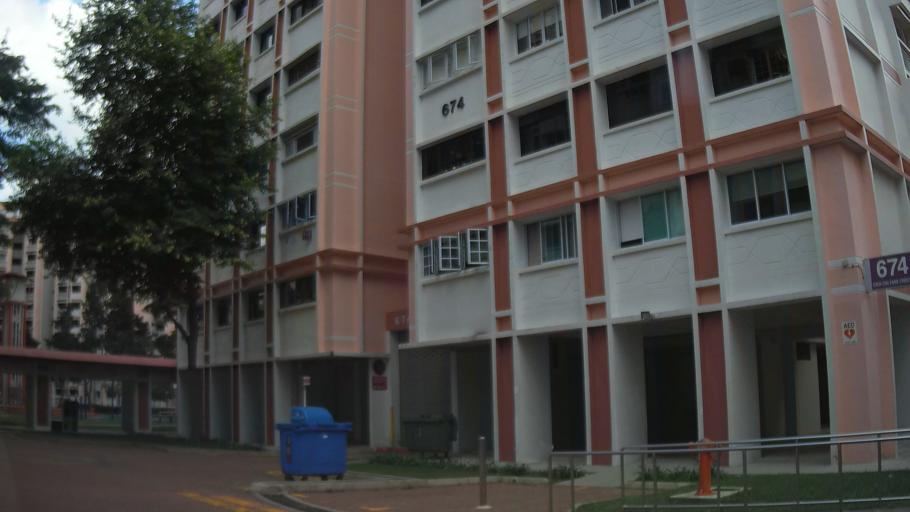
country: MY
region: Johor
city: Johor Bahru
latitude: 1.4019
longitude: 103.7469
